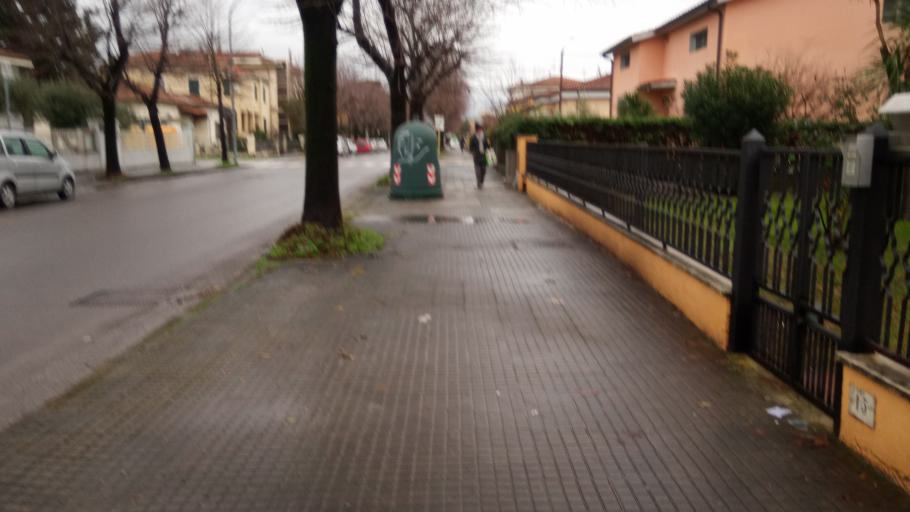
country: IT
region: Tuscany
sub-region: Province of Pisa
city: Pisa
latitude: 43.7192
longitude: 10.4167
